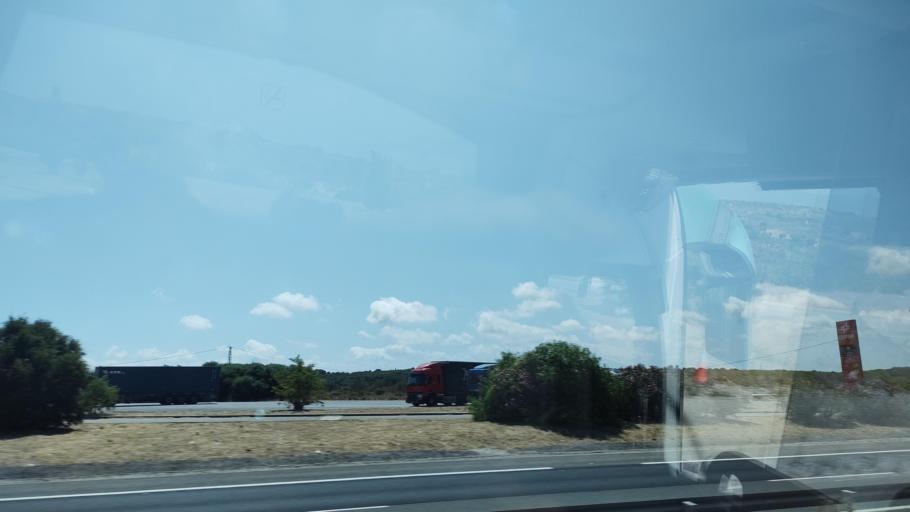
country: ES
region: Andalusia
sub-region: Provincia de Malaga
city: Manilva
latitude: 36.3336
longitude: -5.2673
